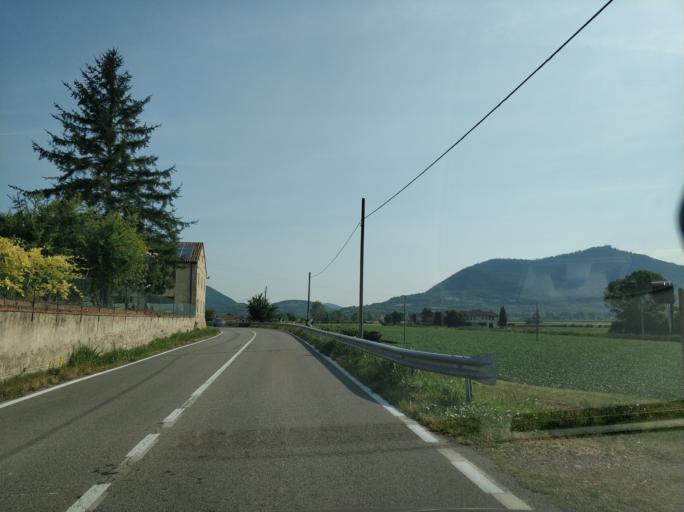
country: IT
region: Veneto
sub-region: Provincia di Padova
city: Baone
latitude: 45.2421
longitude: 11.7110
